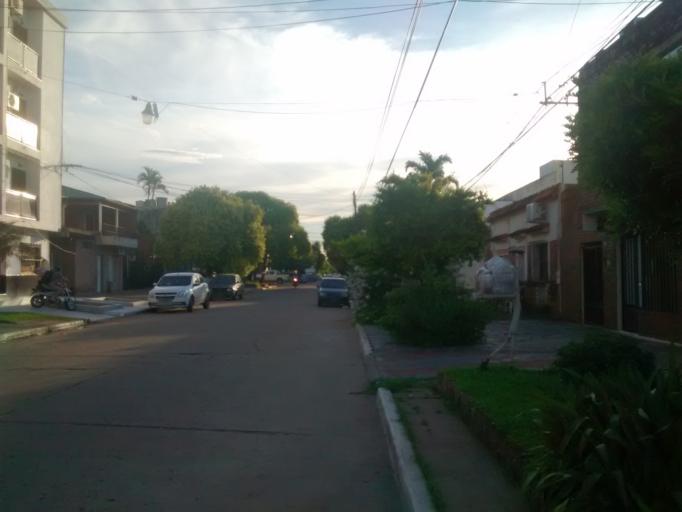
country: AR
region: Chaco
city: Resistencia
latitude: -27.4411
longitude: -58.9930
